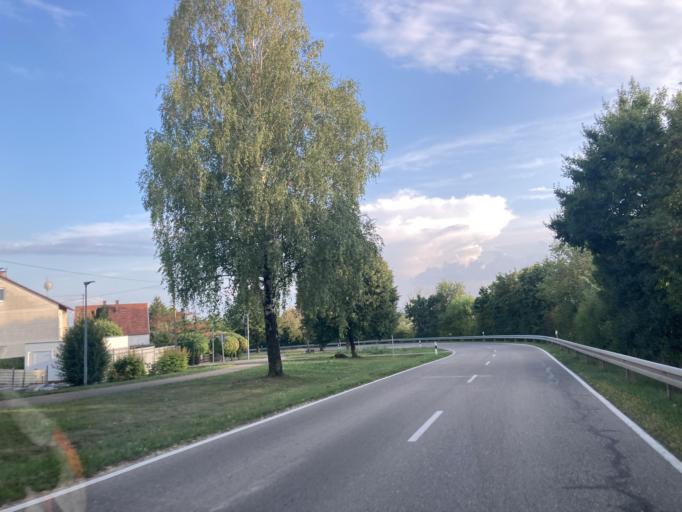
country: DE
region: Bavaria
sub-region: Swabia
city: Medlingen
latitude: 48.5714
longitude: 10.3128
